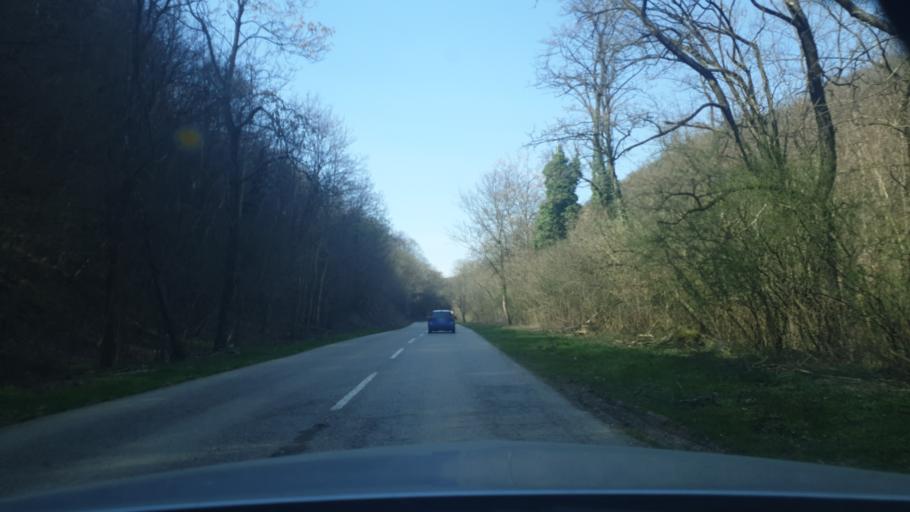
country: RS
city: Vrdnik
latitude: 45.1385
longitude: 19.7753
